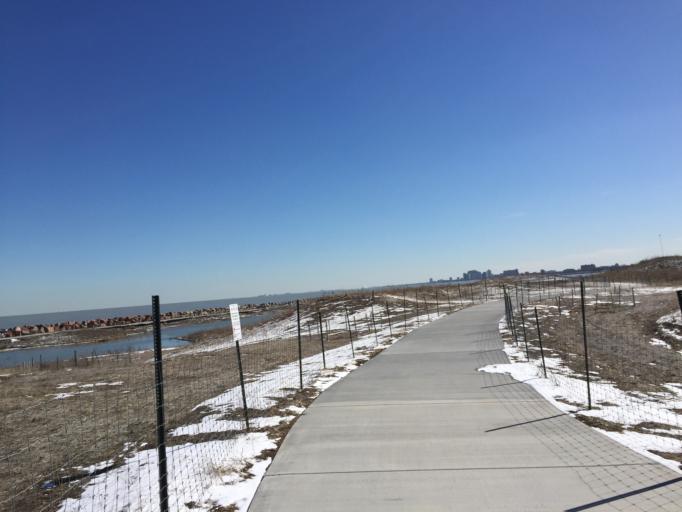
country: US
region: Illinois
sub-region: Cook County
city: Chicago
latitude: 41.8587
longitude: -87.6089
